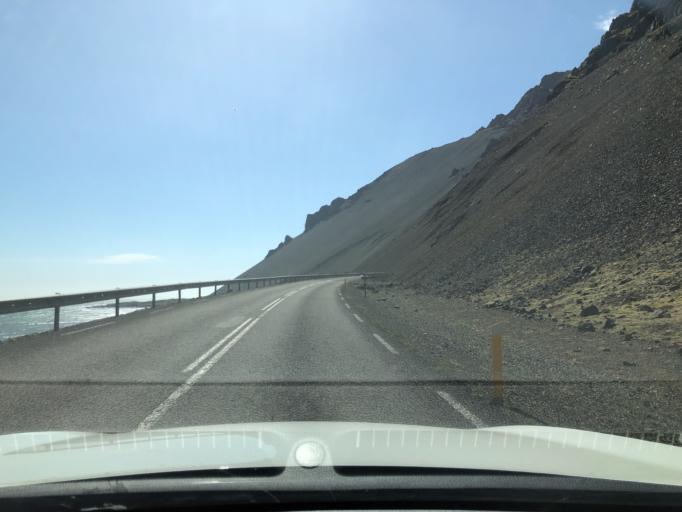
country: IS
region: East
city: Reydarfjoerdur
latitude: 64.4574
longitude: -14.5097
